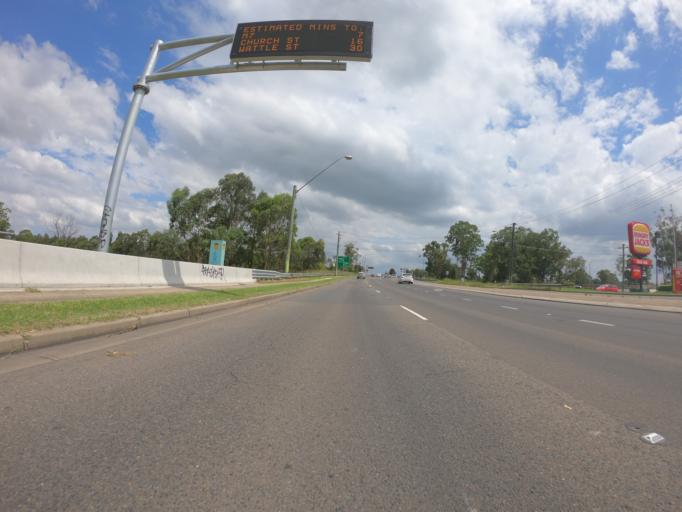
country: AU
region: New South Wales
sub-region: Blacktown
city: Mount Druitt
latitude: -33.7816
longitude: 150.7716
